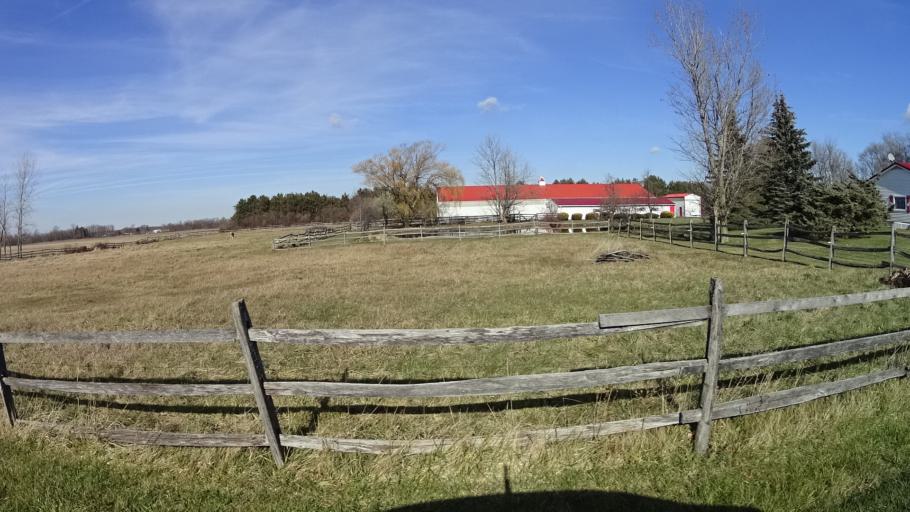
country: US
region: Ohio
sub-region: Lorain County
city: Wellington
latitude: 41.0847
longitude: -82.2137
